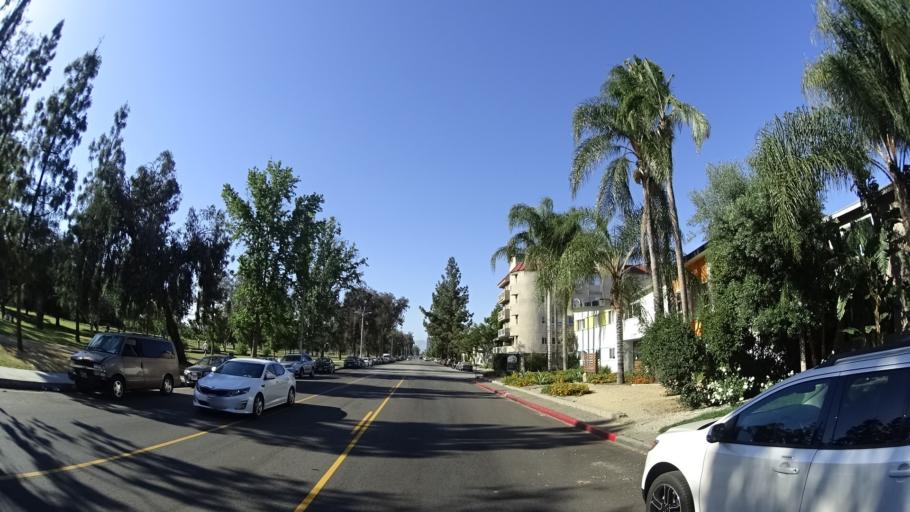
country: US
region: California
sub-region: Los Angeles County
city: North Hollywood
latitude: 34.1603
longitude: -118.3790
